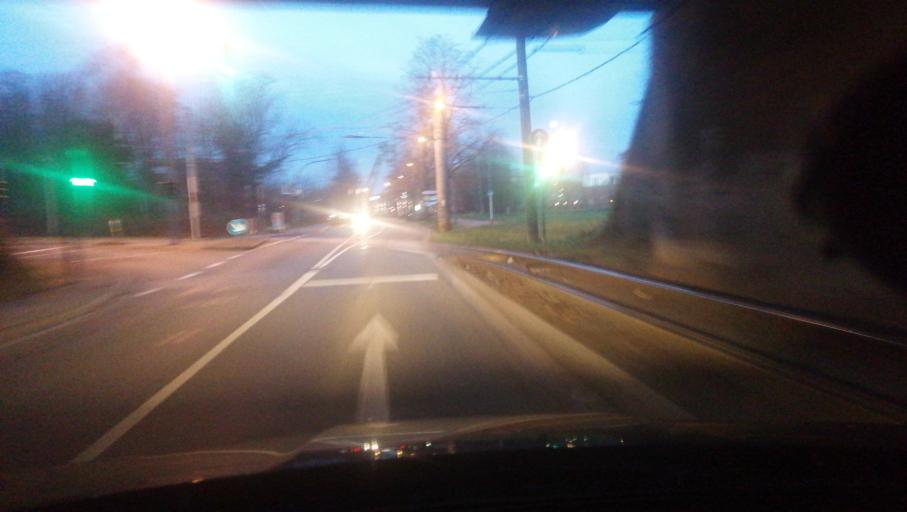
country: DE
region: North Rhine-Westphalia
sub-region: Regierungsbezirk Arnsberg
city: Dortmund
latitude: 51.5340
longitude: 7.4171
